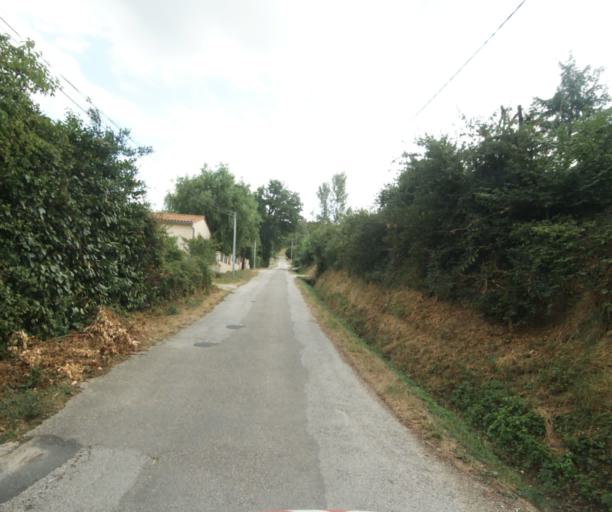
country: FR
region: Midi-Pyrenees
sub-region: Departement de la Haute-Garonne
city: Revel
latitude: 43.4475
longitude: 1.9967
